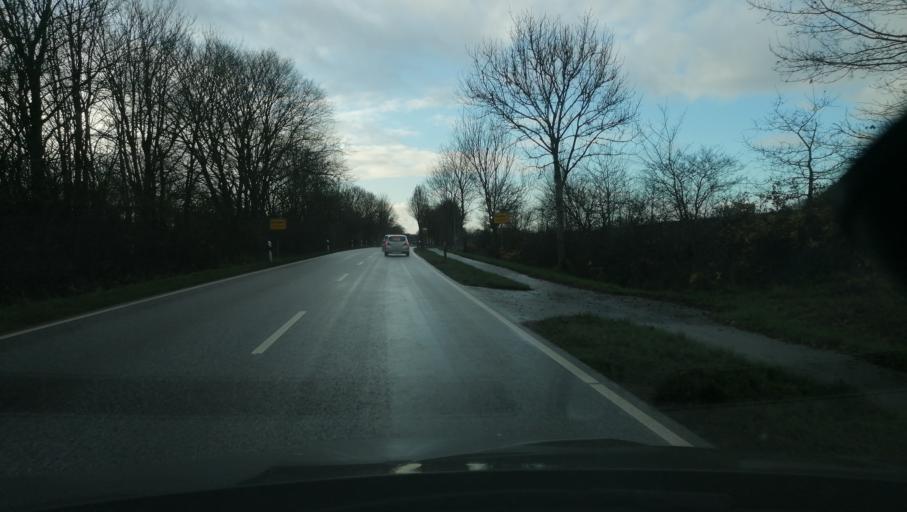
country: DE
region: Schleswig-Holstein
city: Nindorf
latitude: 54.0886
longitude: 9.1305
